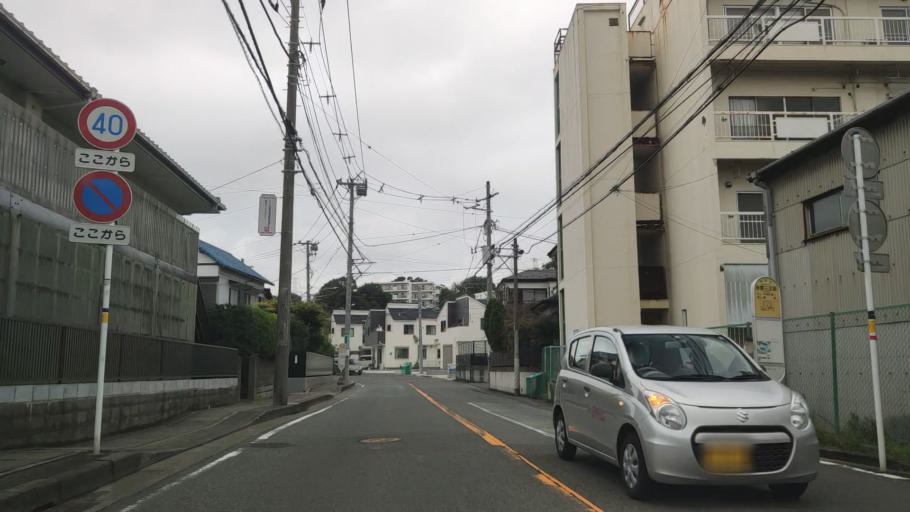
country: JP
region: Kanagawa
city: Yokohama
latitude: 35.4210
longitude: 139.5481
